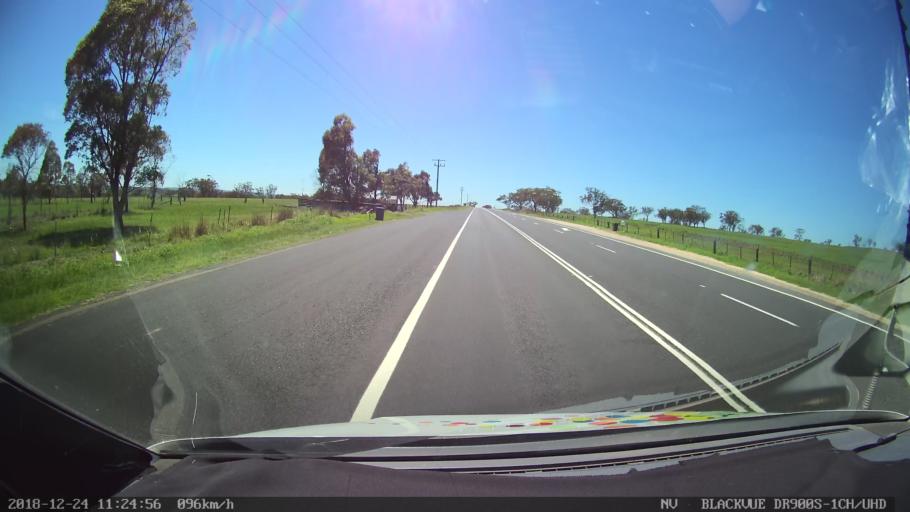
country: AU
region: New South Wales
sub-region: Upper Hunter Shire
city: Merriwa
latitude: -32.1672
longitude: 150.4085
